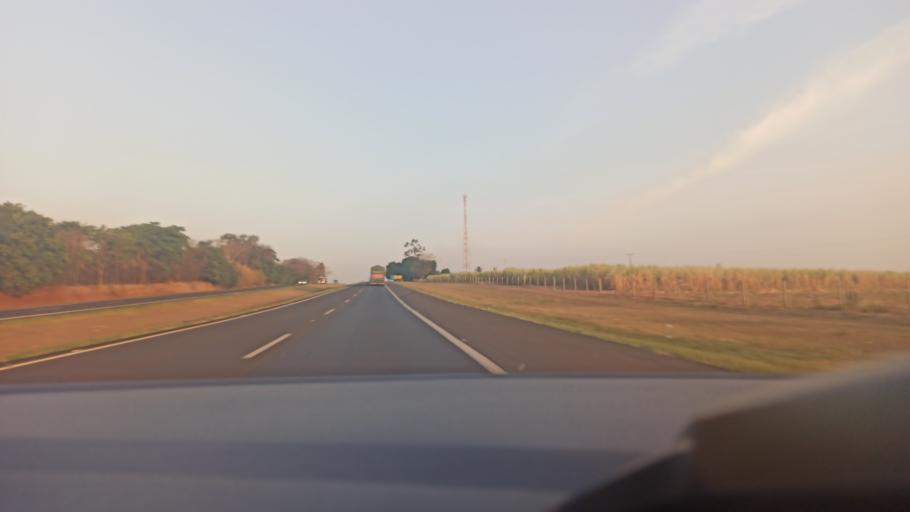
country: BR
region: Sao Paulo
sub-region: Taquaritinga
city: Taquaritinga
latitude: -21.4111
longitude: -48.6919
